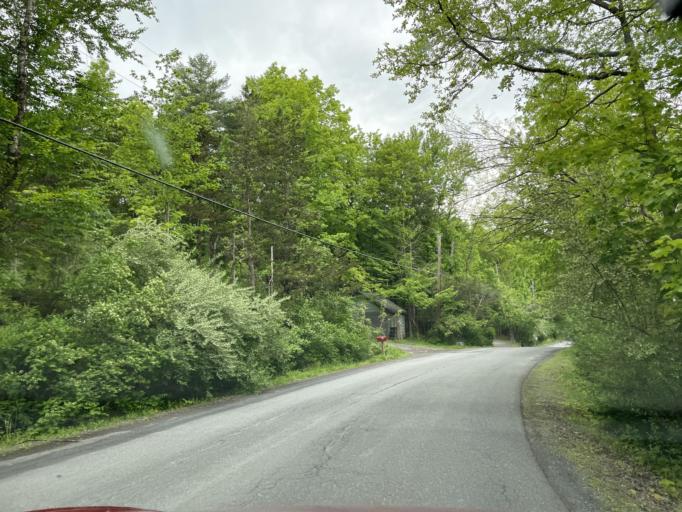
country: US
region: New York
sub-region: Ulster County
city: Woodstock
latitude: 42.0318
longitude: -74.1319
